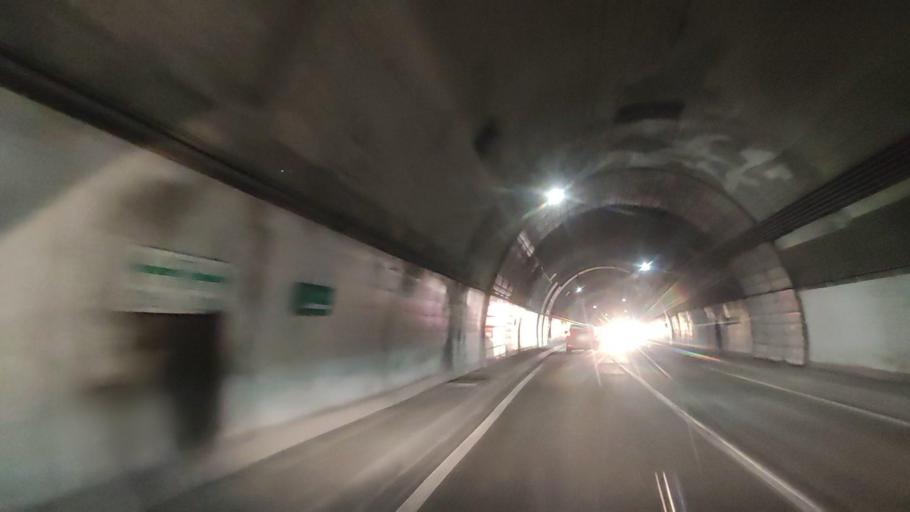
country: JP
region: Hokkaido
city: Ishikari
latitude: 43.4435
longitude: 141.4134
